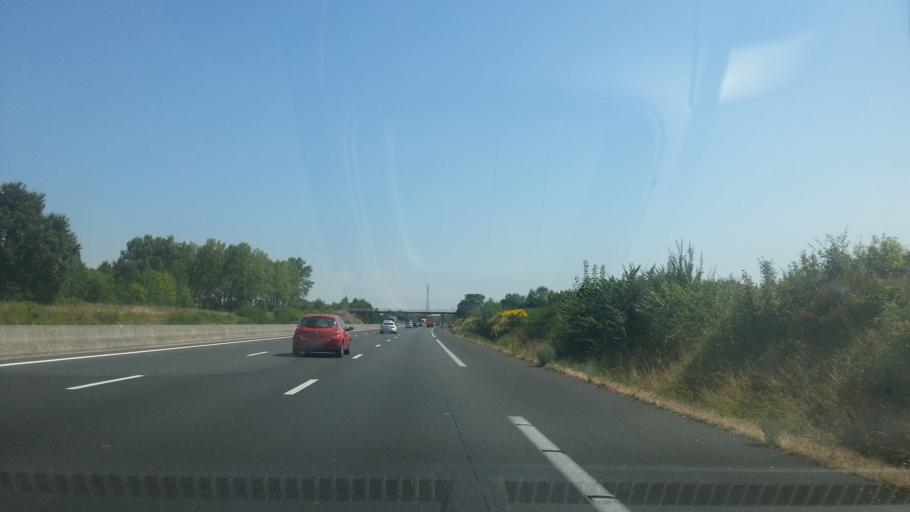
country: FR
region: Centre
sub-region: Departement du Loiret
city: Chaingy
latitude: 47.8908
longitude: 1.7610
